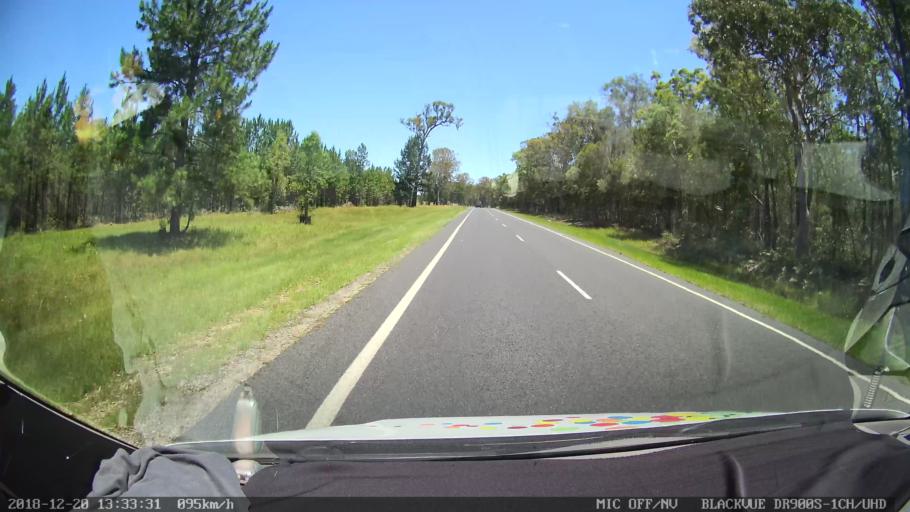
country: AU
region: New South Wales
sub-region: Clarence Valley
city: Gordon
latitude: -29.2465
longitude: 152.9862
